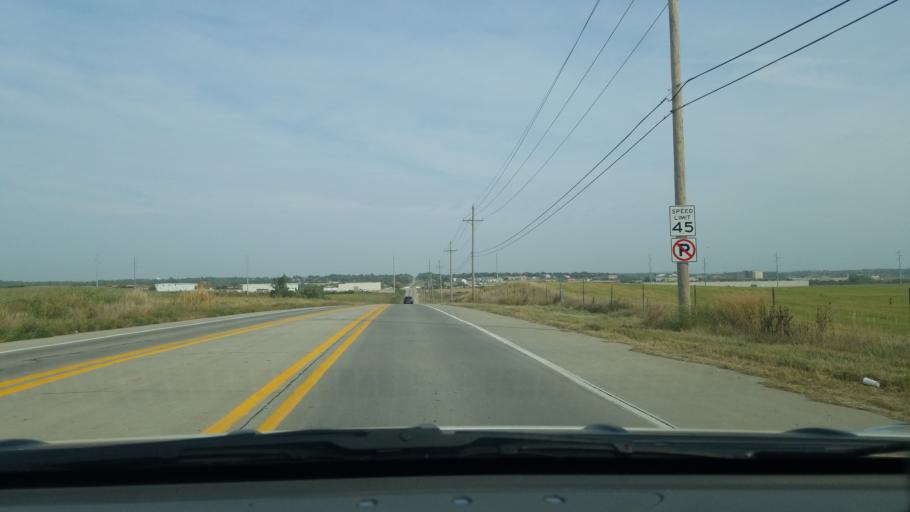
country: US
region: Nebraska
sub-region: Sarpy County
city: Chalco
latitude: 41.1621
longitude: -96.1195
